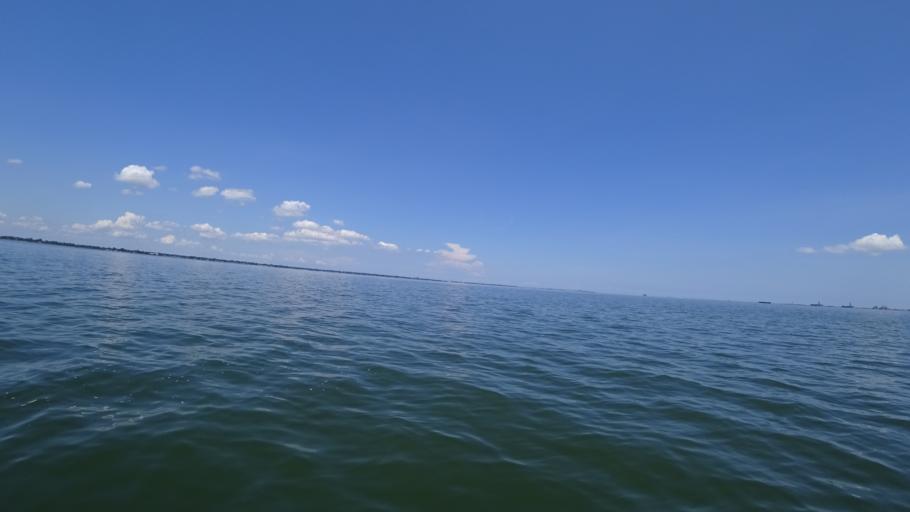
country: US
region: Virginia
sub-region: City of Newport News
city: Newport News
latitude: 36.9550
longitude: -76.3848
